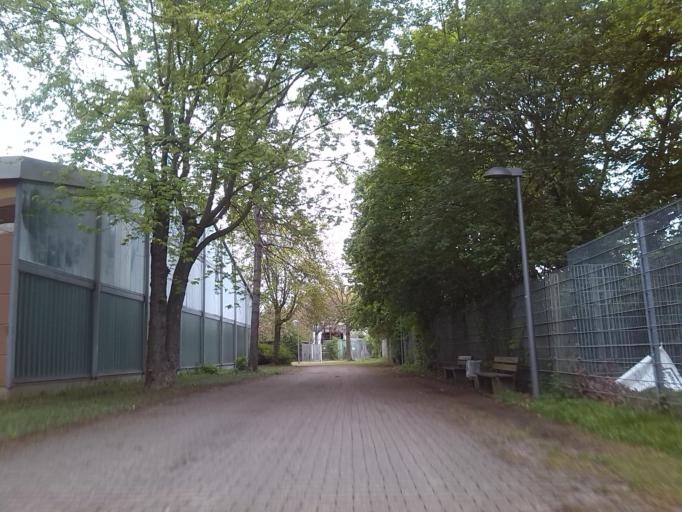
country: DE
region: Baden-Wuerttemberg
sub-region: Karlsruhe Region
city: Mannheim
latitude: 49.4832
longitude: 8.5025
